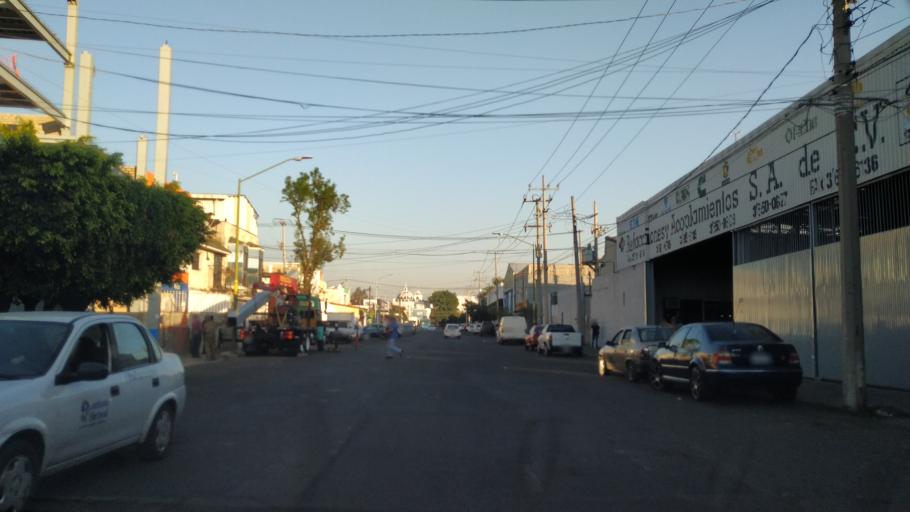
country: MX
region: Jalisco
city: Tlaquepaque
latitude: 20.6579
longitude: -103.3340
